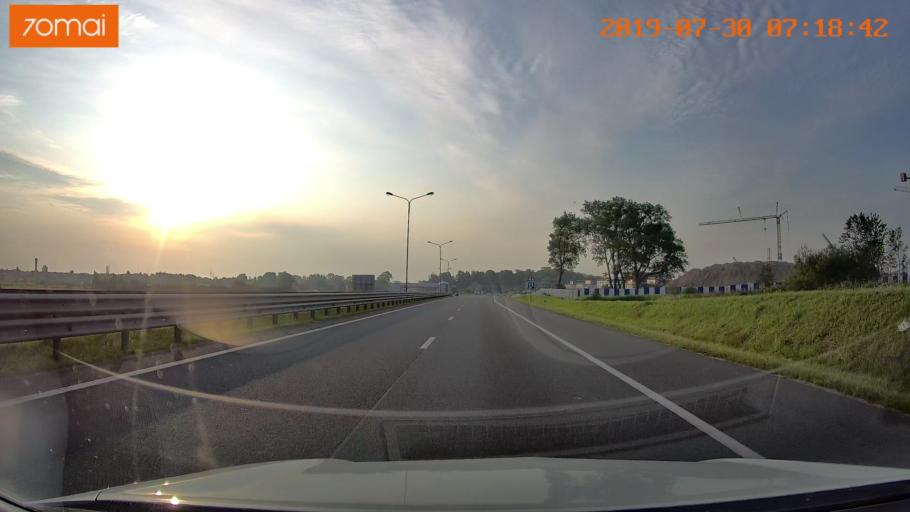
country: RU
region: Kaliningrad
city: Bol'shoe Isakovo
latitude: 54.7029
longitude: 20.6546
